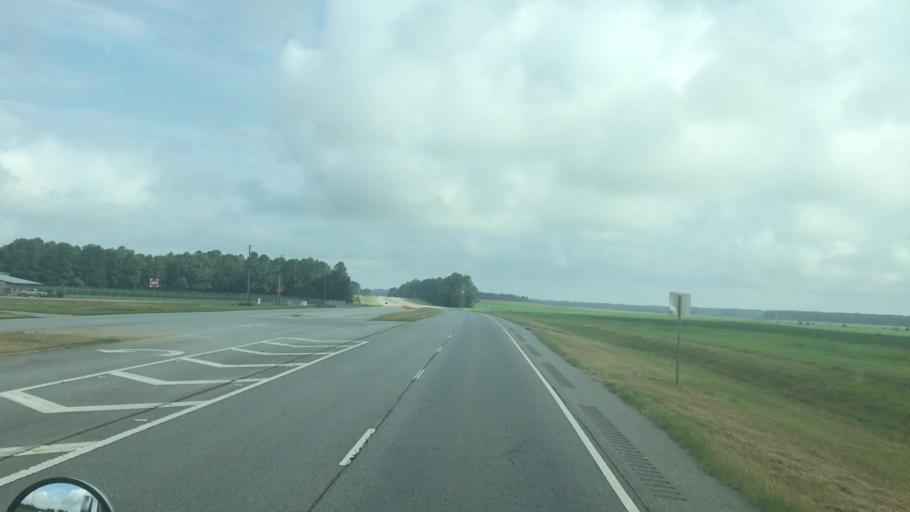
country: US
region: Georgia
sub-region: Miller County
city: Colquitt
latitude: 31.1845
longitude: -84.7624
